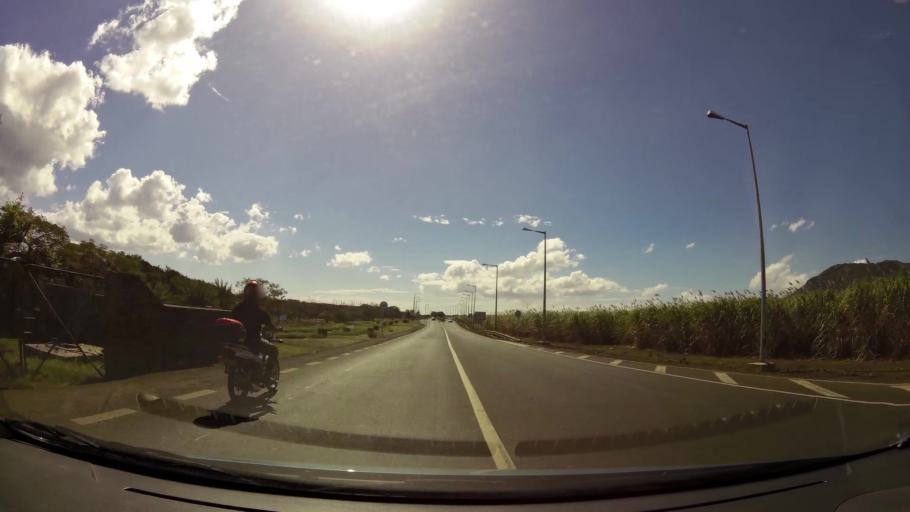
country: MU
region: Black River
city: Cascavelle
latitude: -20.2763
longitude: 57.4051
